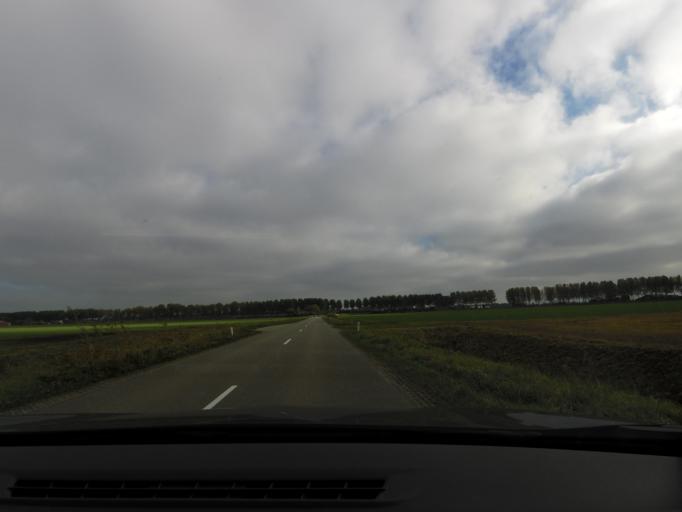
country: NL
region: South Holland
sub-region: Gemeente Oud-Beijerland
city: Oud-Beijerland
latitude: 51.7543
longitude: 4.3856
